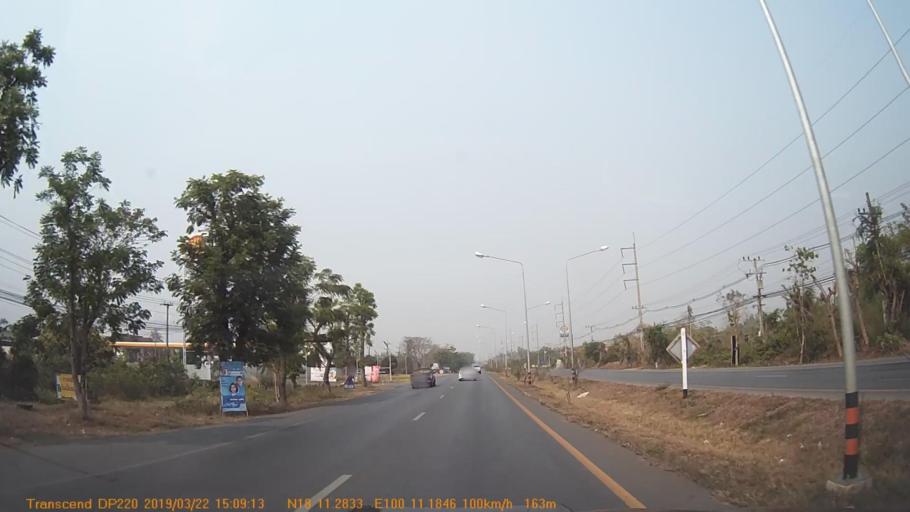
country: TH
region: Phrae
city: Phrae
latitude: 18.1883
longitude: 100.1866
